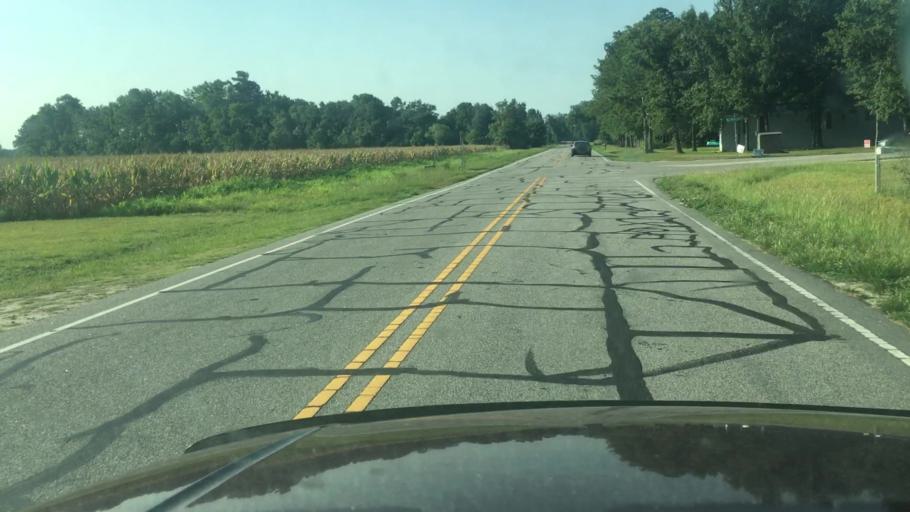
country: US
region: North Carolina
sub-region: Robeson County
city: Saint Pauls
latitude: 34.8359
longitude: -78.8940
